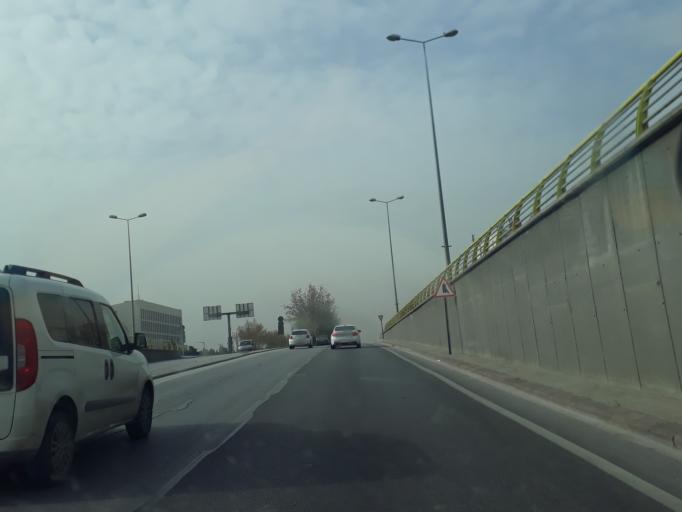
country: TR
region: Konya
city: Selcuklu
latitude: 37.9472
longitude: 32.5125
